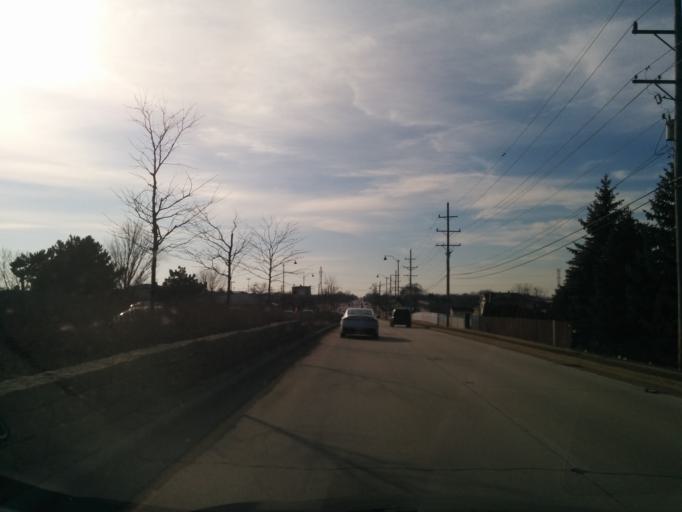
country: US
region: Illinois
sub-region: Cook County
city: Tinley Park
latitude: 41.5802
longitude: -87.8097
